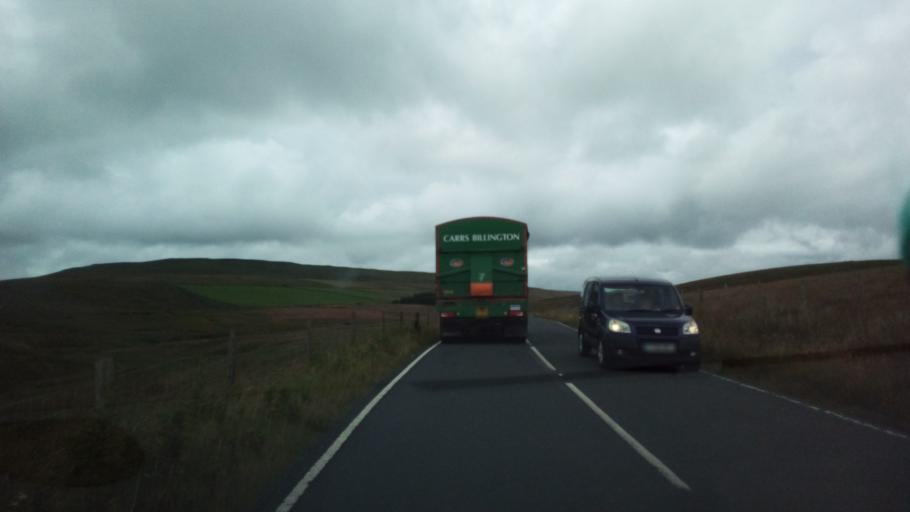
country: GB
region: England
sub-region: North Yorkshire
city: Ingleton
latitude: 54.2444
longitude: -2.3163
